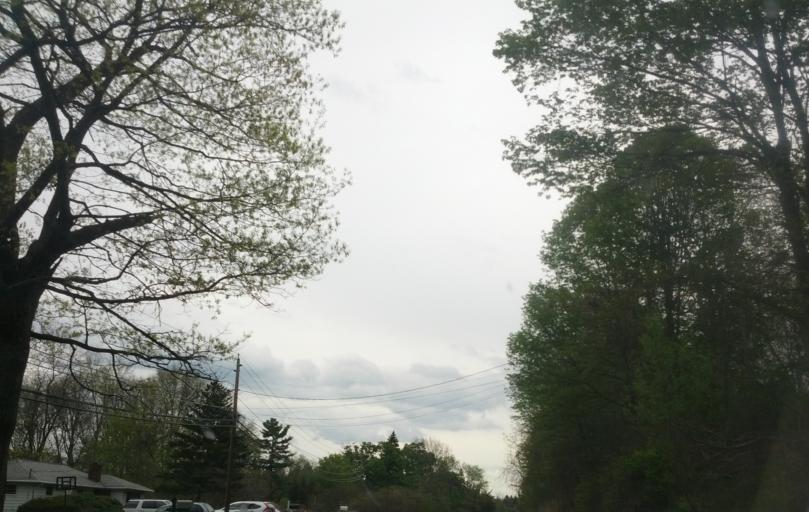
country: US
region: New York
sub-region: Onondaga County
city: Nedrow
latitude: 42.9959
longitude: -76.1059
